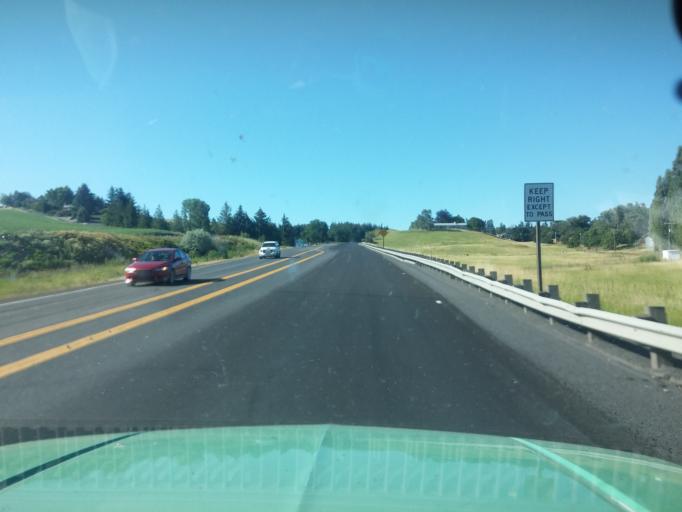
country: US
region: Idaho
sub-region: Latah County
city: Moscow
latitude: 46.6986
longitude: -117.0075
